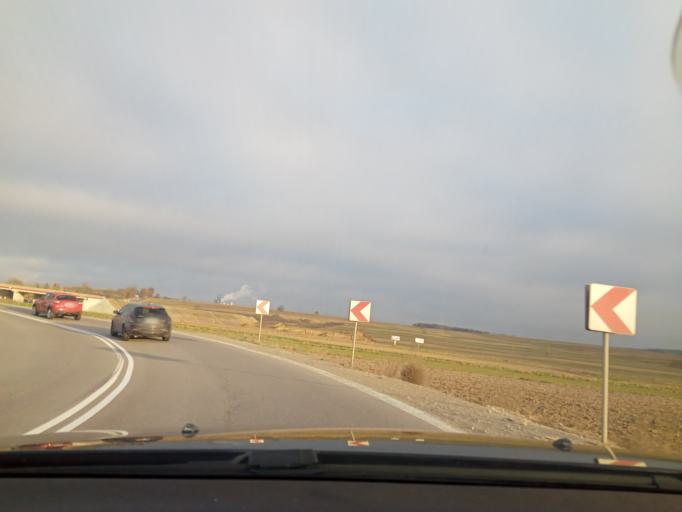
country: PL
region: Lesser Poland Voivodeship
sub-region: Powiat miechowski
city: Miechow
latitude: 50.3134
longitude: 20.0403
